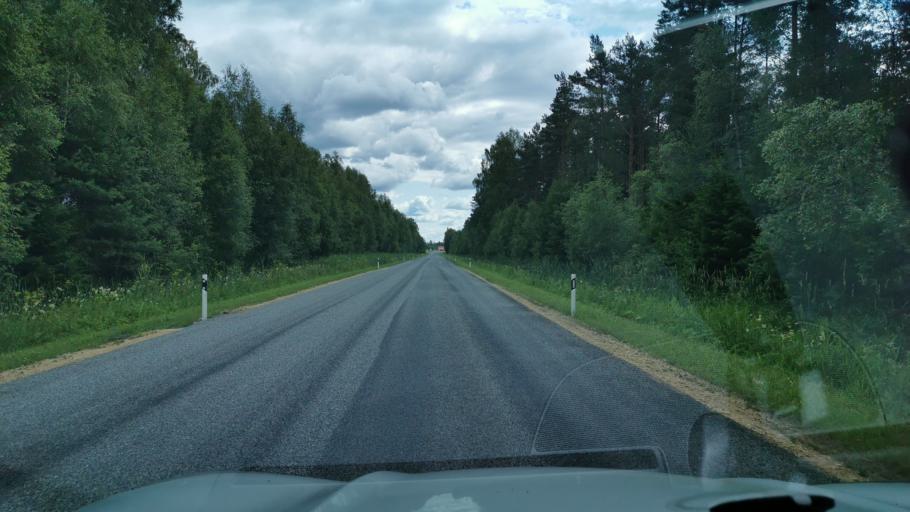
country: EE
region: Harju
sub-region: Anija vald
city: Kehra
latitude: 59.2379
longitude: 25.3753
